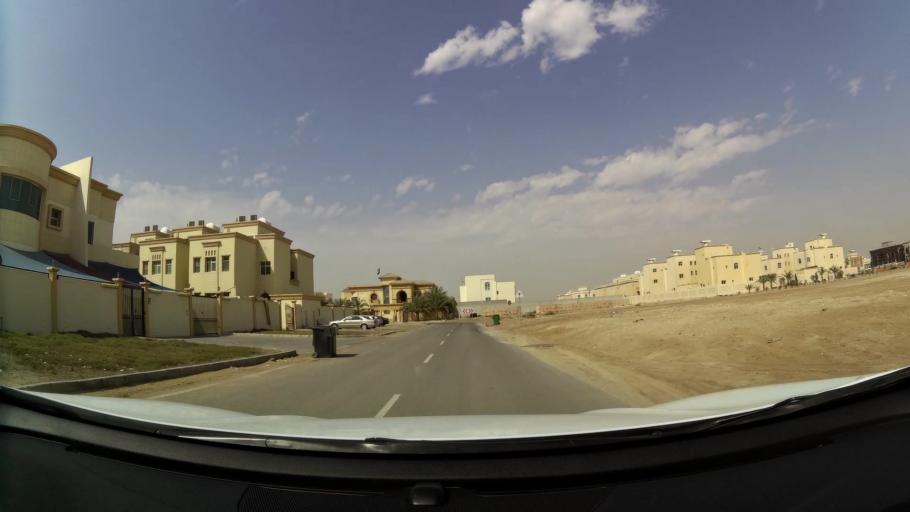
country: AE
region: Abu Dhabi
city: Abu Dhabi
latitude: 24.3312
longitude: 54.5461
